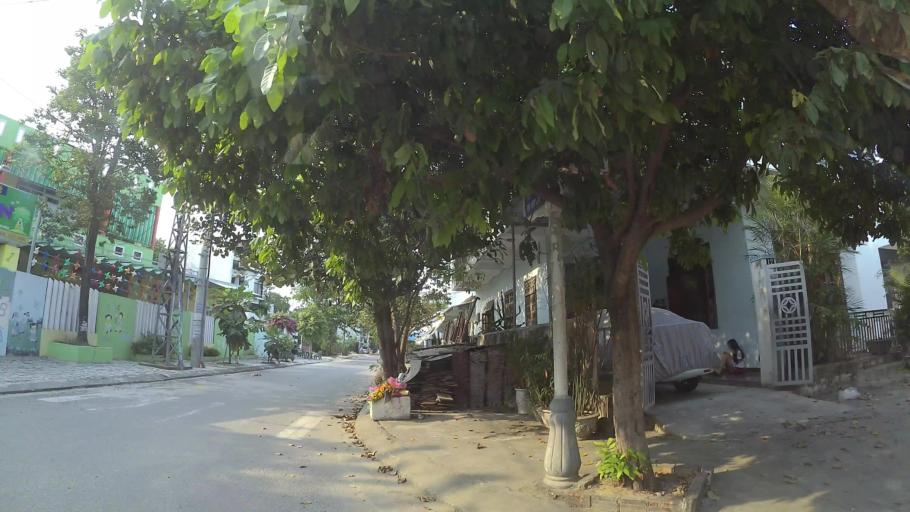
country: VN
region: Da Nang
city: Cam Le
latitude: 16.0213
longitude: 108.2060
